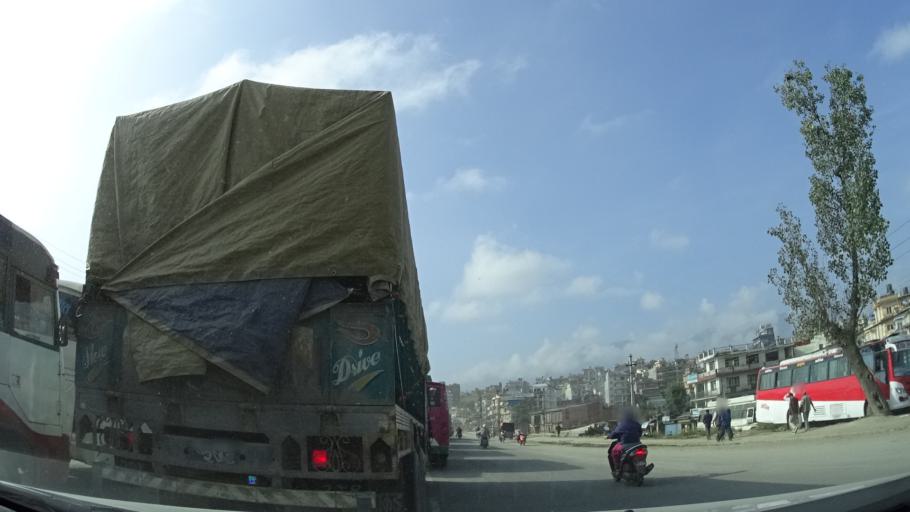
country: NP
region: Central Region
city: Kirtipur
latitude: 27.7010
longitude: 85.2818
